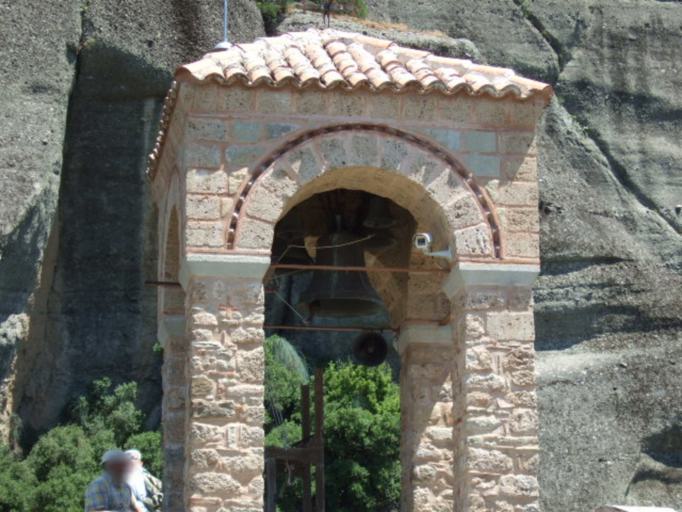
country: GR
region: Thessaly
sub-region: Trikala
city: Kastraki
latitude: 39.7238
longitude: 21.6246
